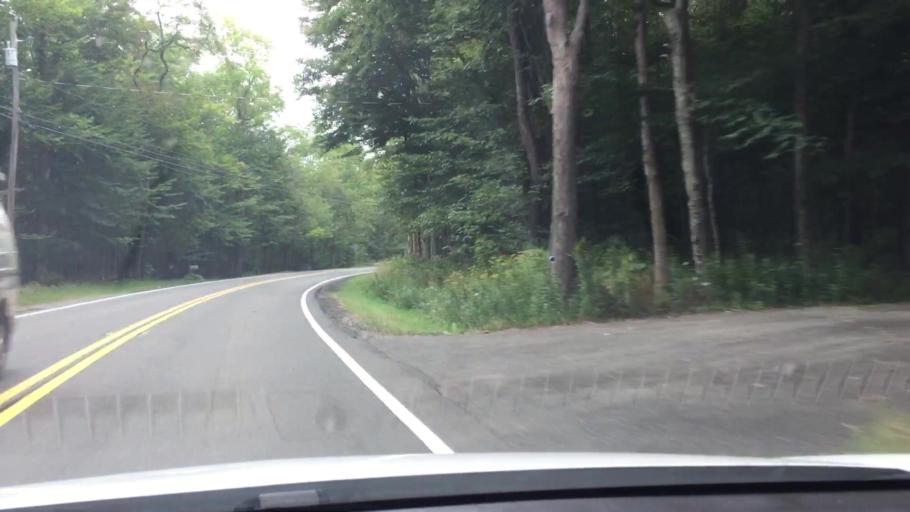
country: US
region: Massachusetts
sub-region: Berkshire County
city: Becket
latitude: 42.3487
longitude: -73.0923
